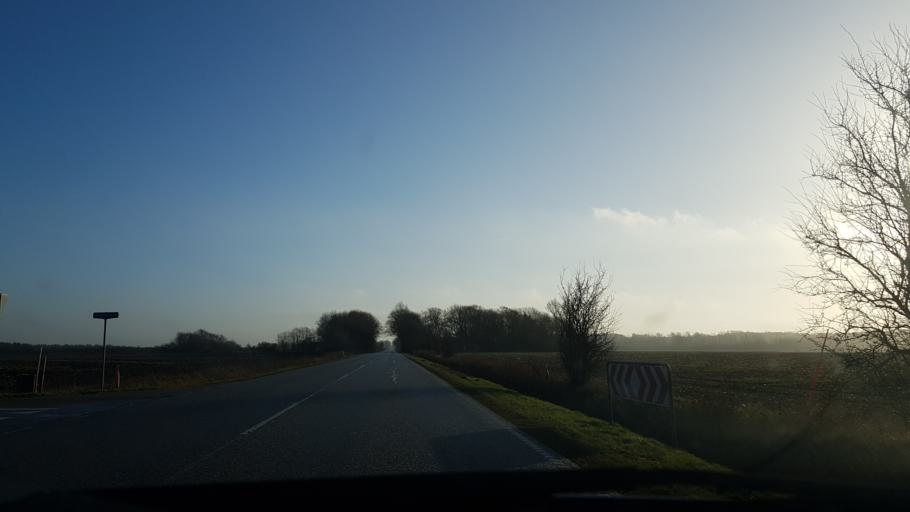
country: DK
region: South Denmark
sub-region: Tonder Kommune
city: Toftlund
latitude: 55.2368
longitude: 9.1630
